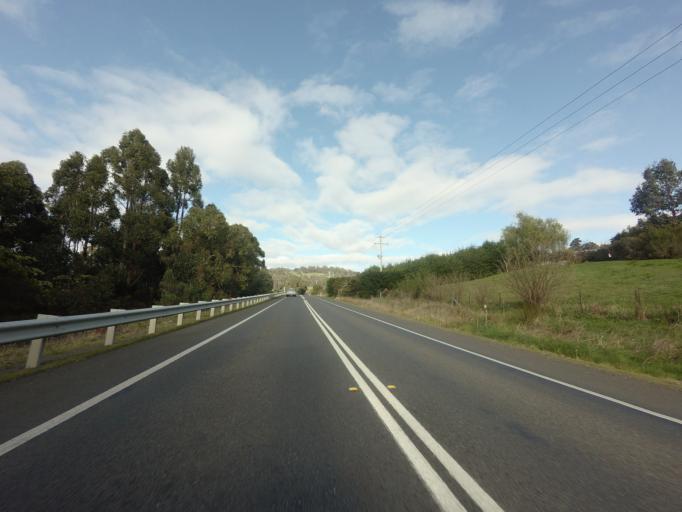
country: AU
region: Tasmania
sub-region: Huon Valley
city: Franklin
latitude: -43.1105
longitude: 146.9989
